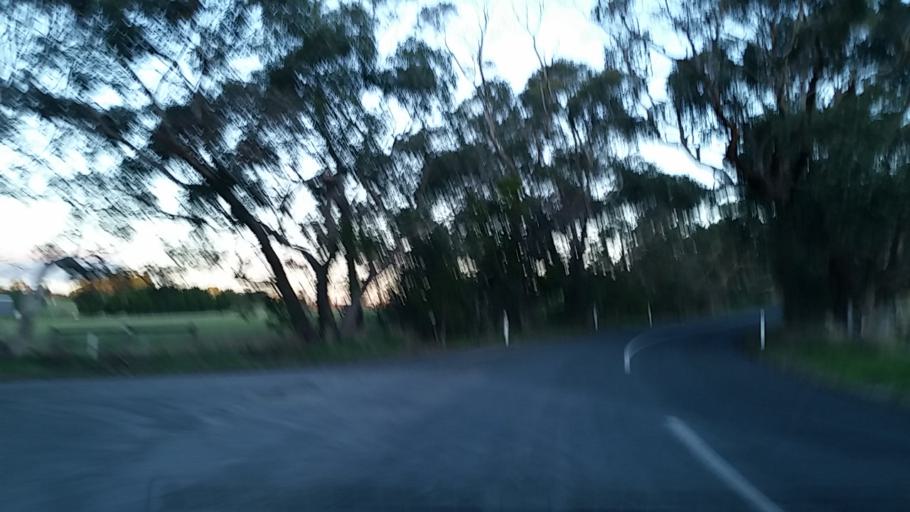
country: AU
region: South Australia
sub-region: Alexandrina
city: Mount Compass
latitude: -35.2899
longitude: 138.6085
